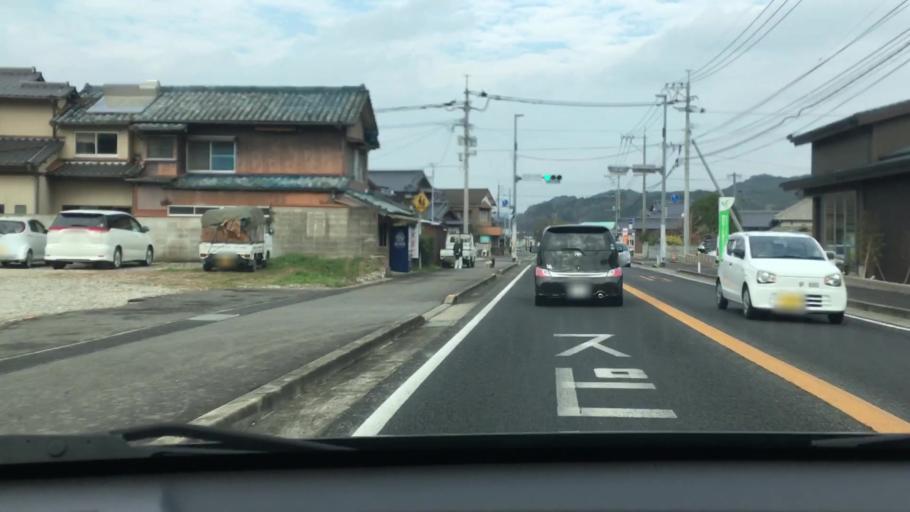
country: JP
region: Saga Prefecture
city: Imaricho-ko
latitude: 33.3105
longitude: 129.9280
